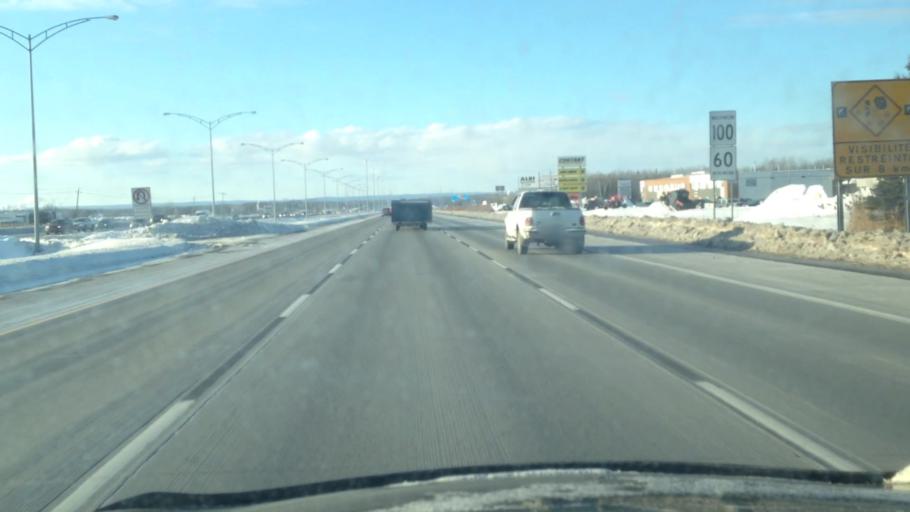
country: CA
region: Quebec
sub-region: Laurentides
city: Blainville
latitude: 45.6849
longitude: -73.9251
